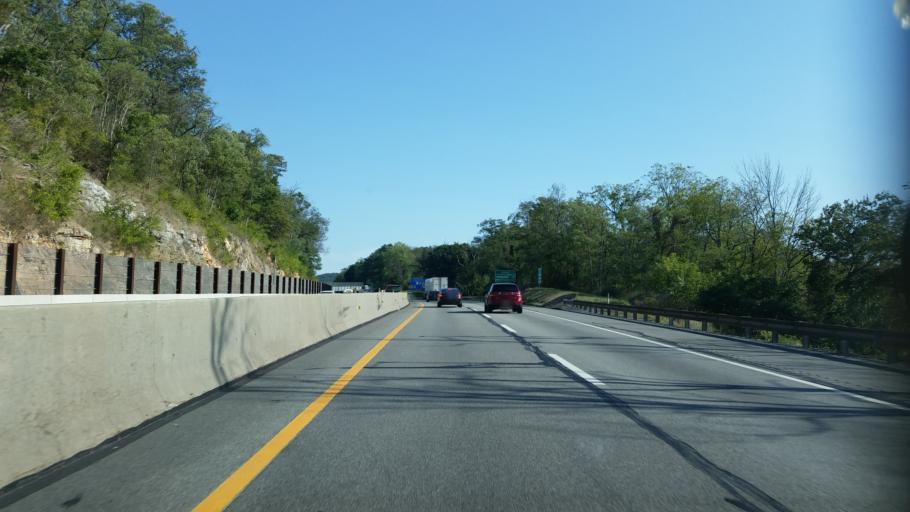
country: US
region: Pennsylvania
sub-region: Bedford County
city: Bedford
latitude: 40.0410
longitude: -78.5044
